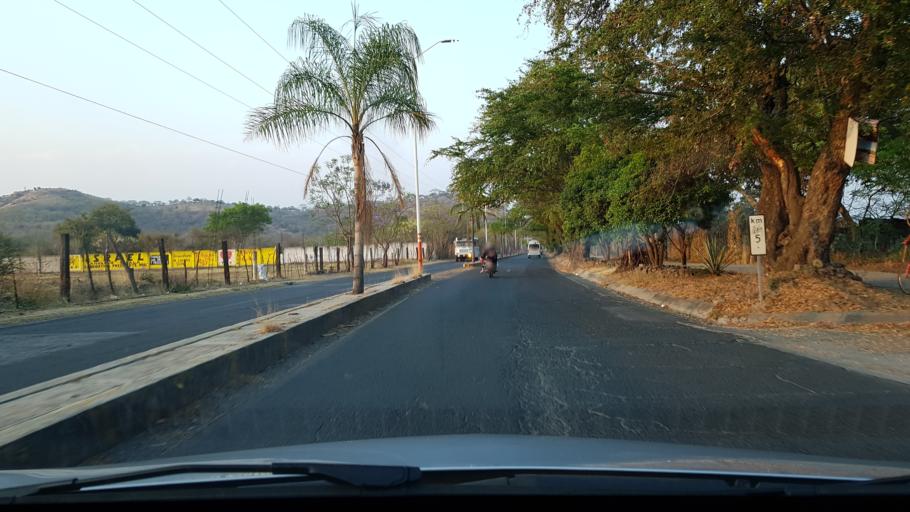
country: MX
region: Morelos
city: Jonacatepec de Leandro Valle
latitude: 18.6734
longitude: -98.8048
